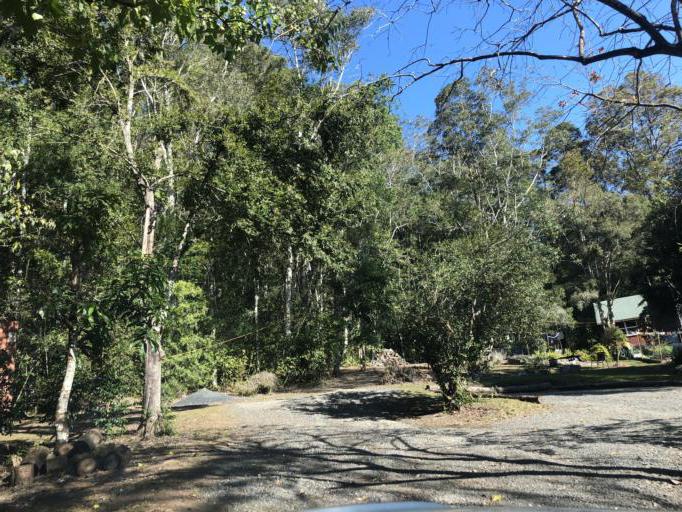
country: AU
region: New South Wales
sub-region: Bellingen
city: Bellingen
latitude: -30.4380
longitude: 152.8264
